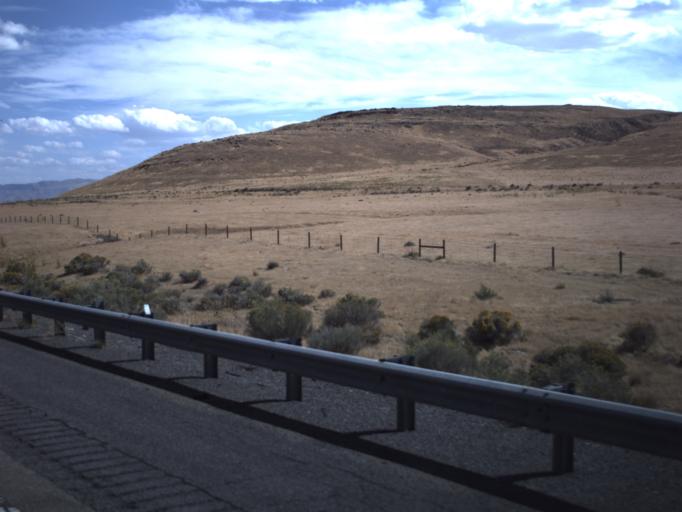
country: US
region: Utah
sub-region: Tooele County
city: Grantsville
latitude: 40.8223
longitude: -112.8924
